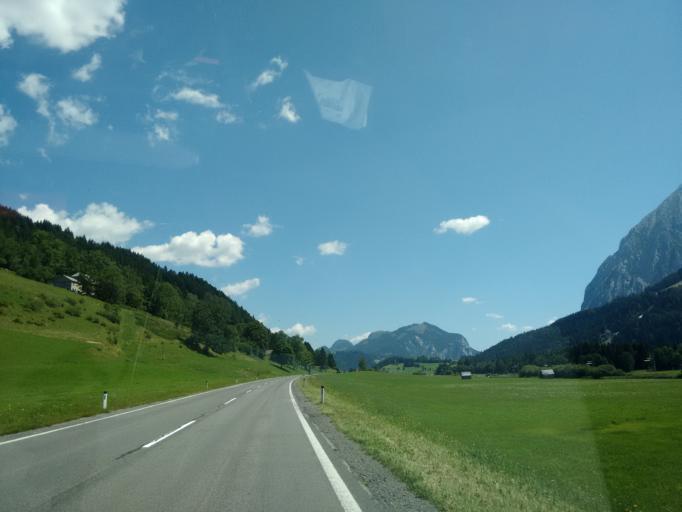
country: AT
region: Styria
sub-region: Politischer Bezirk Liezen
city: Tauplitz
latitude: 47.5526
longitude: 13.9772
